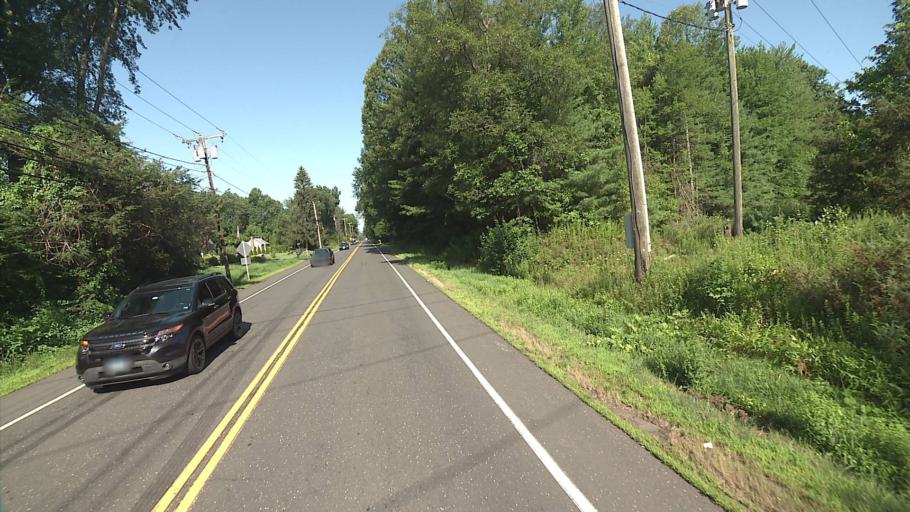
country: US
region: Connecticut
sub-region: Hartford County
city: Salmon Brook
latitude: 41.9534
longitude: -72.7691
